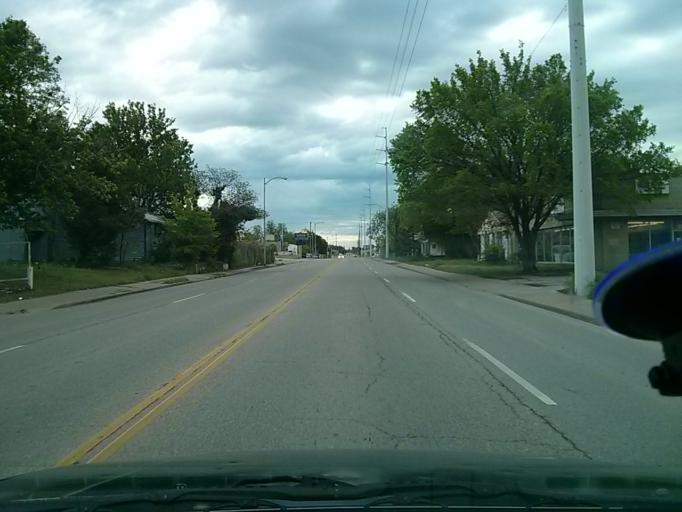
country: US
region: Oklahoma
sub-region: Tulsa County
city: Tulsa
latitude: 36.1567
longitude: -95.9714
